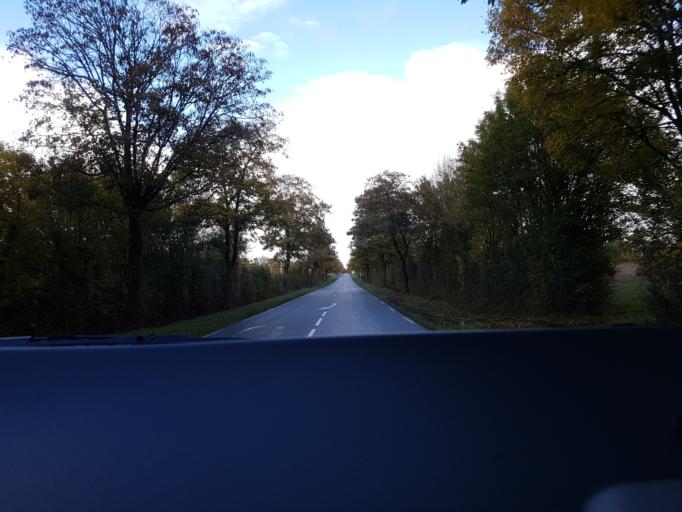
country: FR
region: Poitou-Charentes
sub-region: Departement des Deux-Sevres
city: Brioux-sur-Boutonne
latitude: 46.0881
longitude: -0.2910
